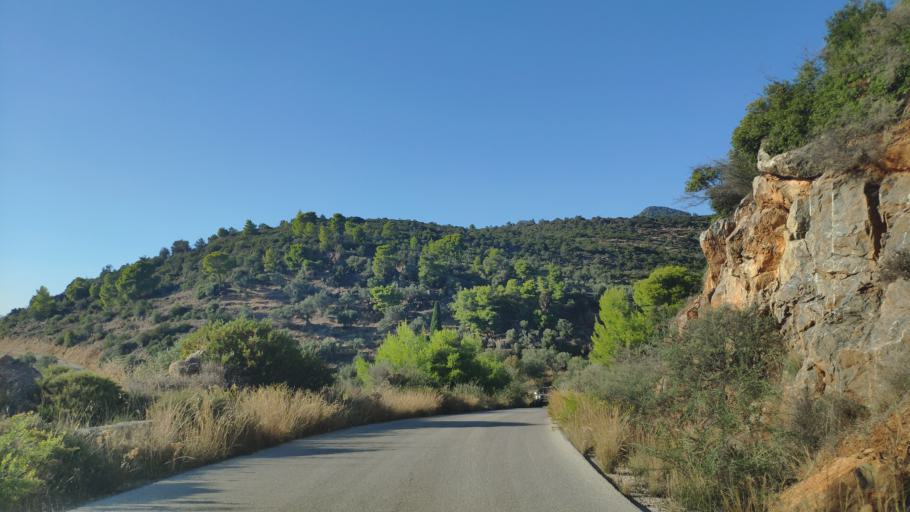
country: GR
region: Attica
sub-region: Nomos Piraios
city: Galatas
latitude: 37.5777
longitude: 23.3585
